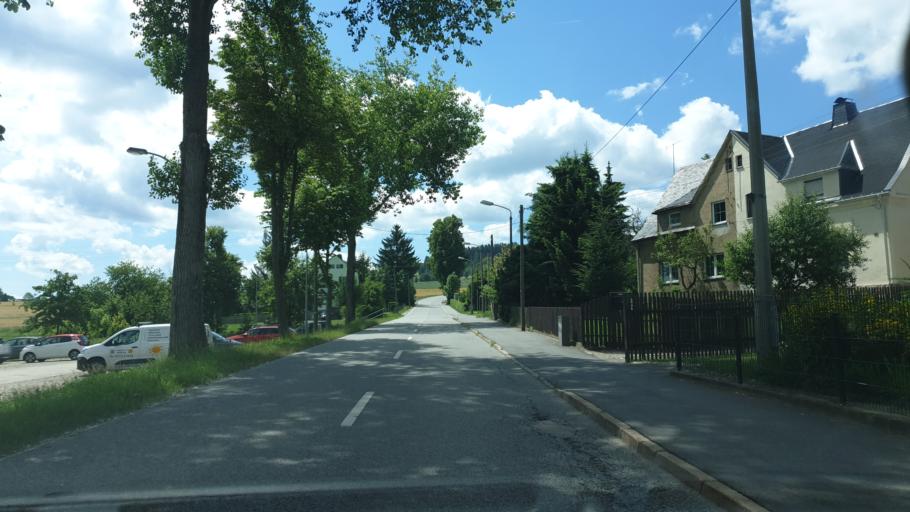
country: DE
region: Saxony
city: Schwarzenberg
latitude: 50.5311
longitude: 12.7698
